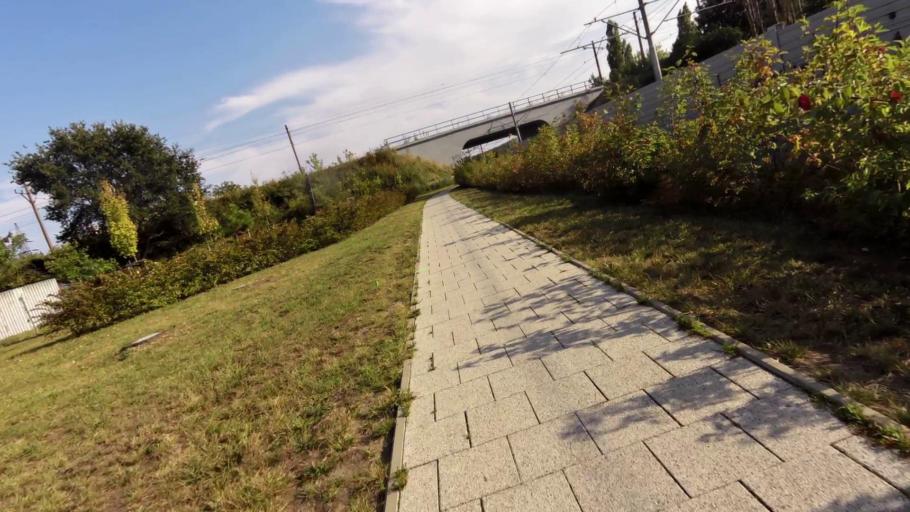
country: PL
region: West Pomeranian Voivodeship
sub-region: Szczecin
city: Szczecin
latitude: 53.3816
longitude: 14.6415
